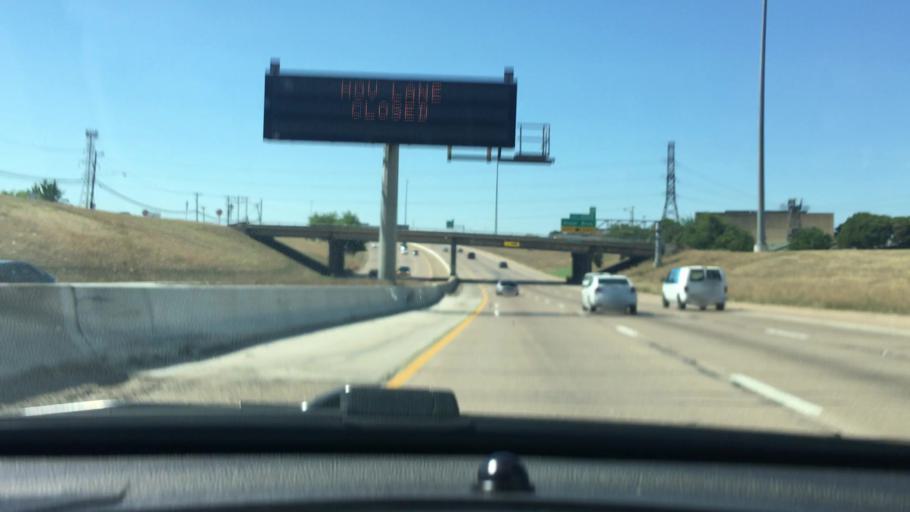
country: US
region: Texas
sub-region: Dallas County
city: Cockrell Hill
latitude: 32.6999
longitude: -96.8239
